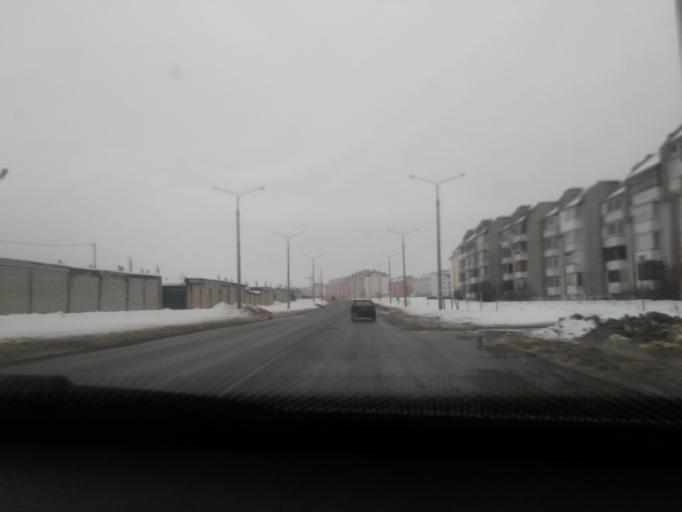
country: BY
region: Mogilev
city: Babruysk
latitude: 53.1919
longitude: 29.2206
